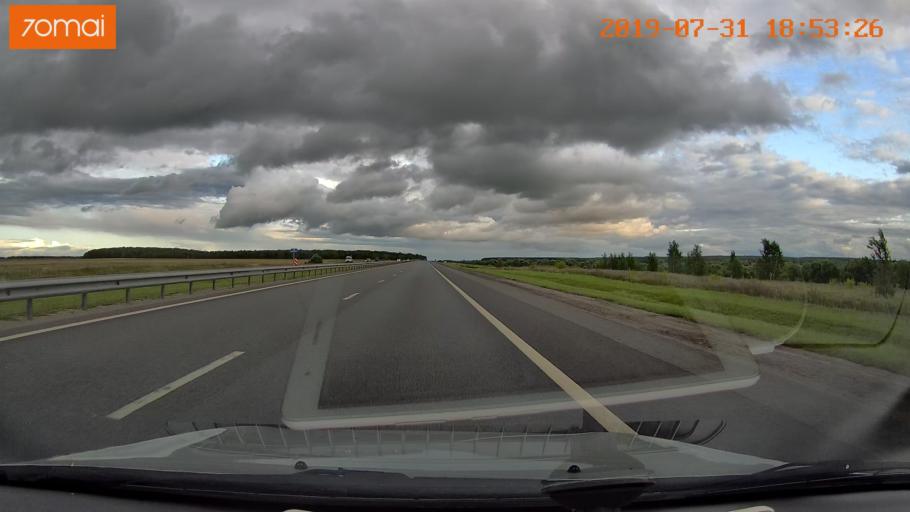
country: RU
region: Moskovskaya
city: Raduzhnyy
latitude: 55.2029
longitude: 38.6531
